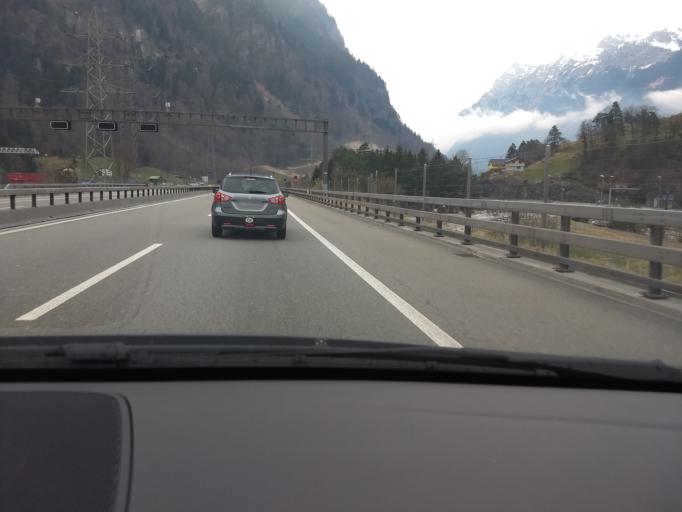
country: CH
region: Uri
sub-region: Uri
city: Silenen
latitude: 46.7711
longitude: 8.6687
